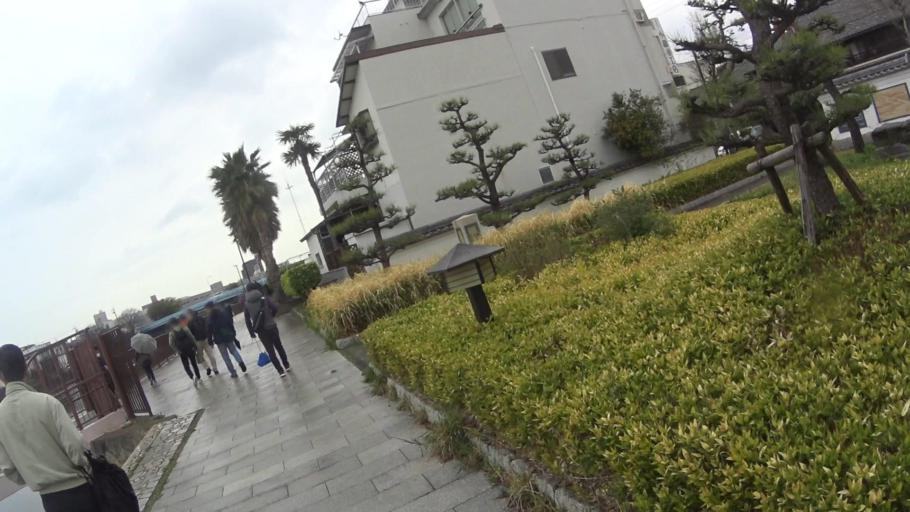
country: JP
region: Aichi
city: Nagoya-shi
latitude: 35.1189
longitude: 136.9049
